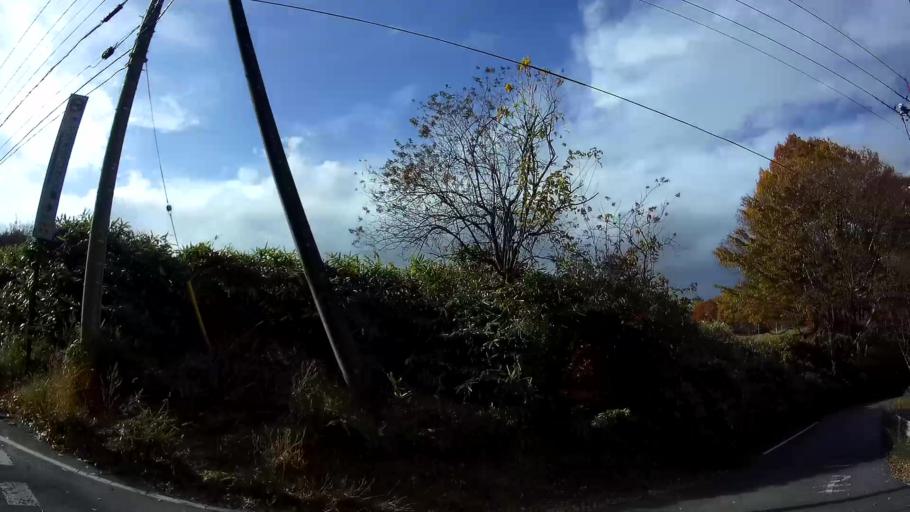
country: JP
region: Gunma
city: Nakanojomachi
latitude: 36.6219
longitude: 138.6317
